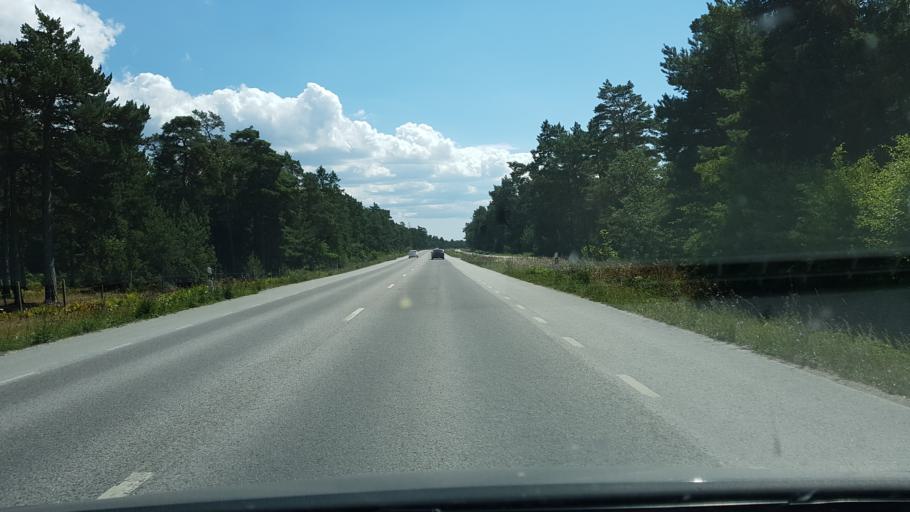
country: SE
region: Gotland
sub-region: Gotland
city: Vibble
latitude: 57.5577
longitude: 18.2024
